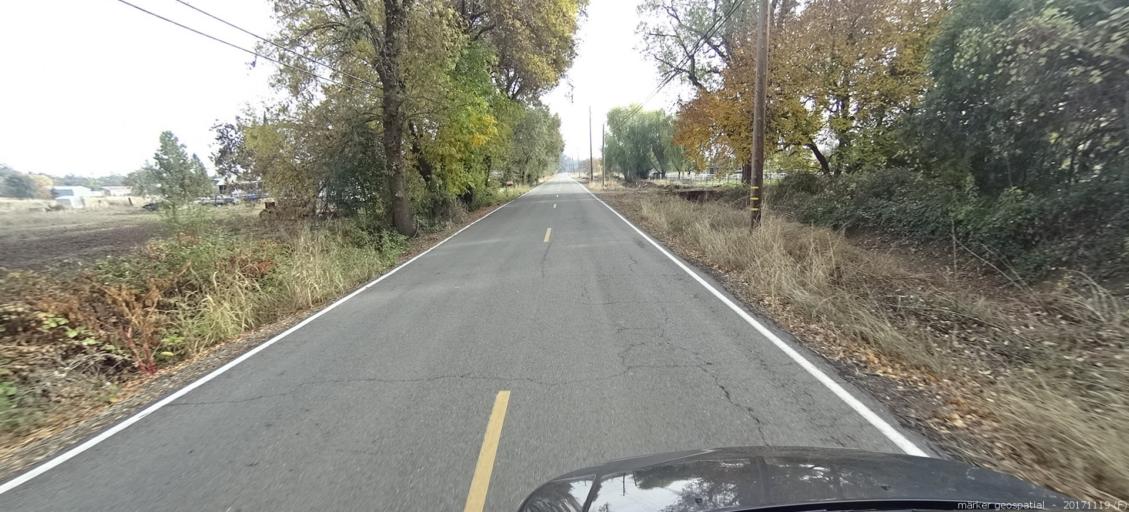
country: US
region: California
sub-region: Shasta County
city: Anderson
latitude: 40.5201
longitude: -122.3391
